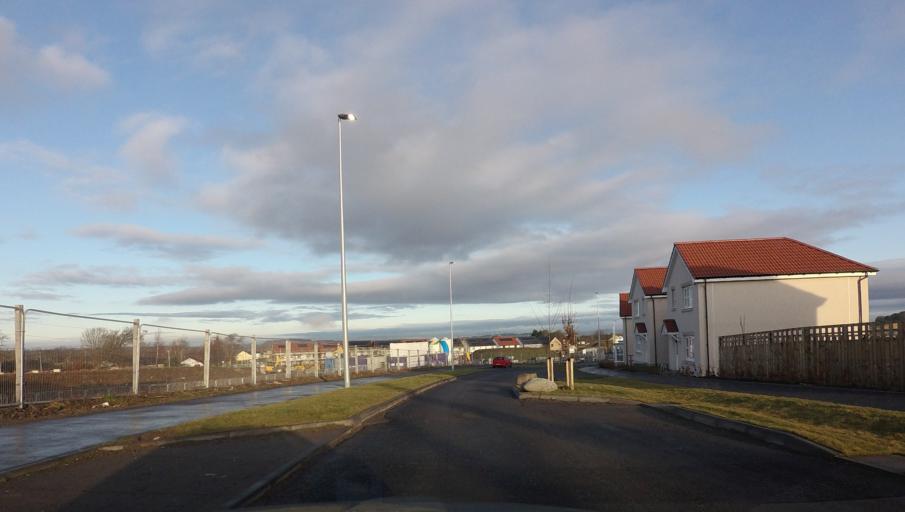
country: GB
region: Scotland
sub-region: West Lothian
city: East Calder
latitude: 55.8994
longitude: -3.4439
